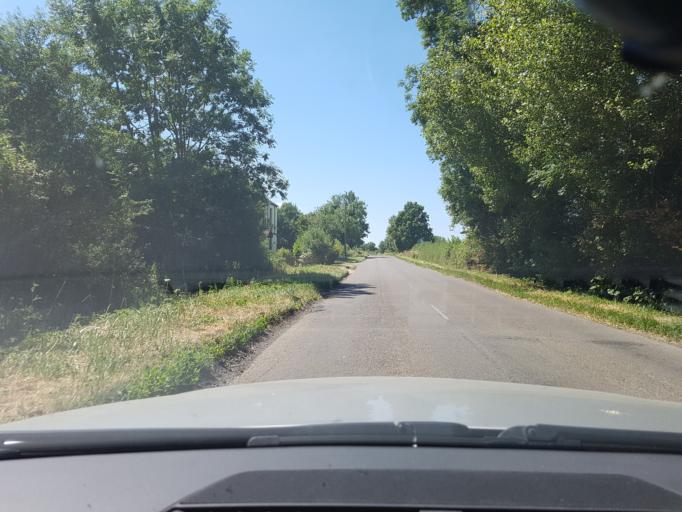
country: GB
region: England
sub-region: Milton Keynes
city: Calverton
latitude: 52.0354
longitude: -0.8280
